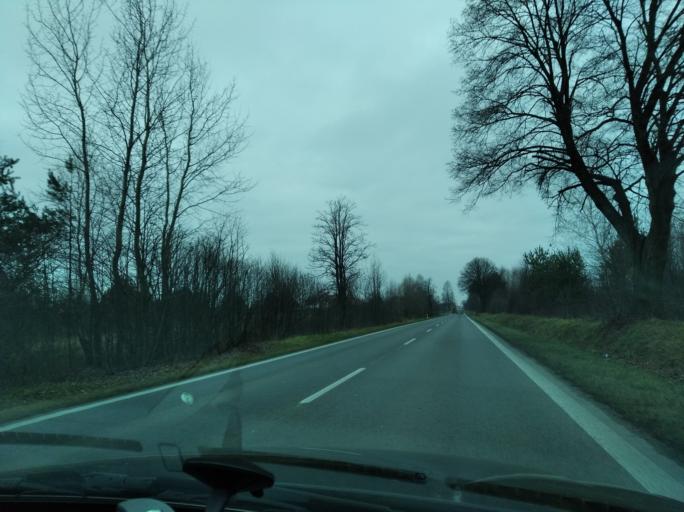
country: PL
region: Subcarpathian Voivodeship
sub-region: Powiat lancucki
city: Zolynia
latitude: 50.1570
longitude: 22.2955
